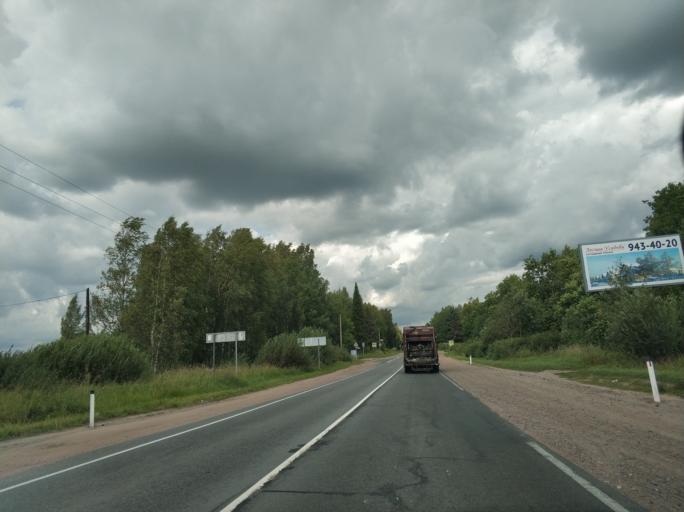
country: RU
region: Leningrad
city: Romanovka
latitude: 60.0604
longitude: 30.7423
